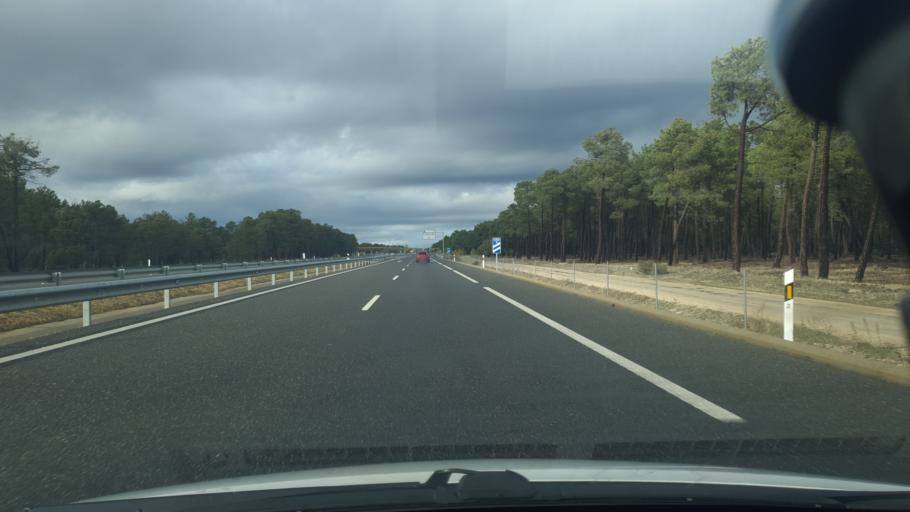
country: ES
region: Castille and Leon
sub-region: Provincia de Segovia
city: Pinarejos
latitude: 41.2431
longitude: -4.2815
